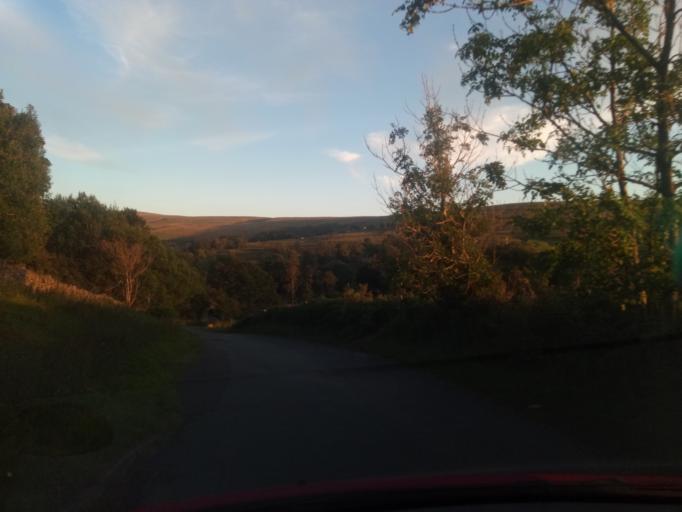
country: GB
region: England
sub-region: Northumberland
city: Bardon Mill
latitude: 54.8083
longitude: -2.3764
